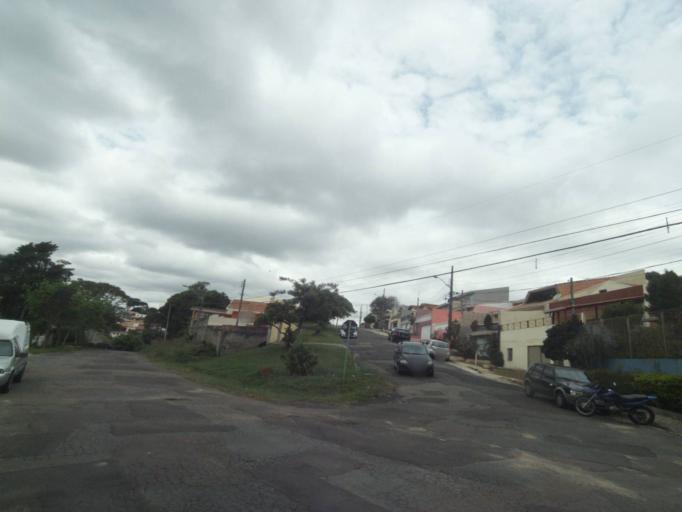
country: BR
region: Parana
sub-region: Curitiba
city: Curitiba
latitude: -25.3897
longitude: -49.2881
